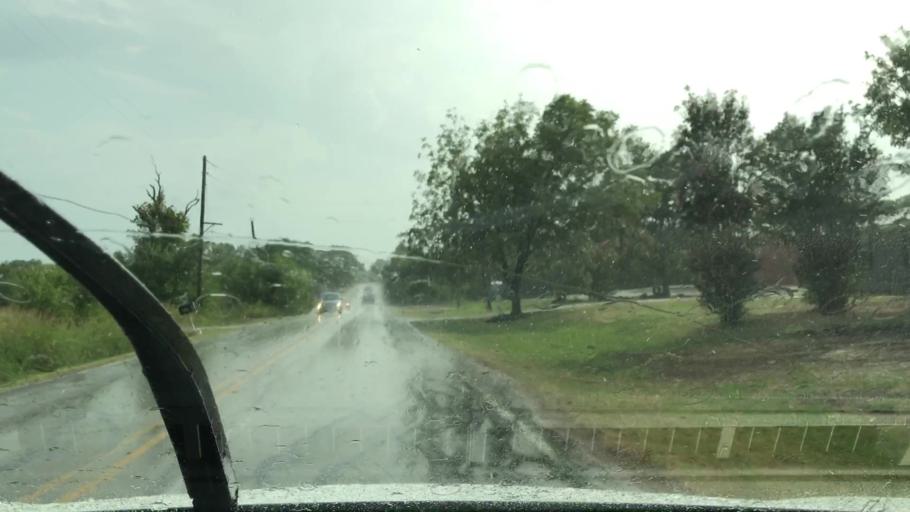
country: US
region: Texas
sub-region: Collin County
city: Wylie
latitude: 32.9643
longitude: -96.5291
